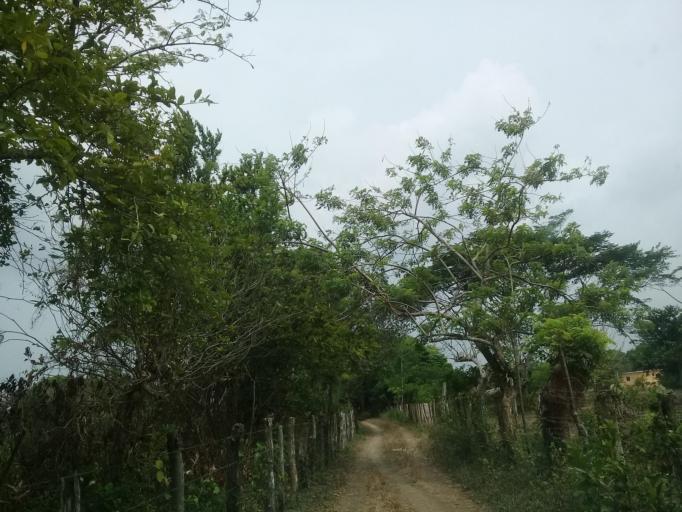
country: MX
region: Veracruz
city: El Tejar
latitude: 19.0568
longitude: -96.1967
